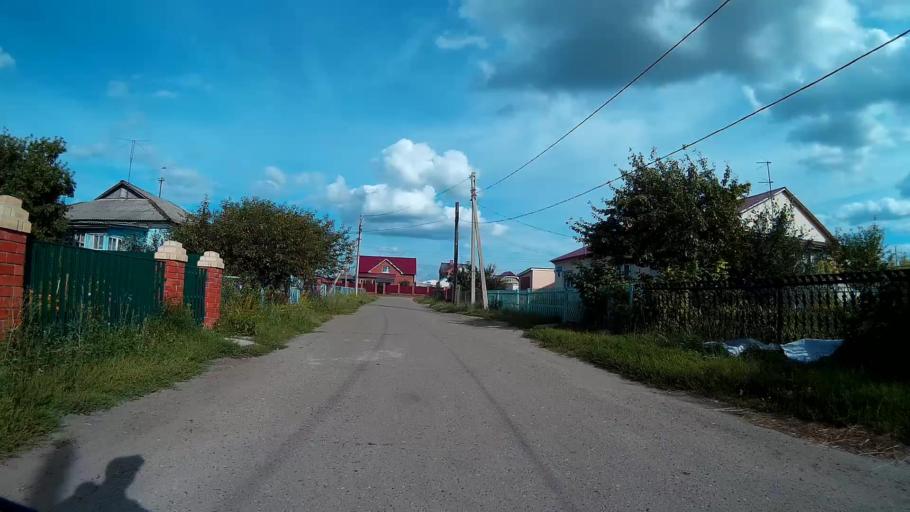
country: RU
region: Ulyanovsk
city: Isheyevka
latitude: 54.2873
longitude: 48.2132
